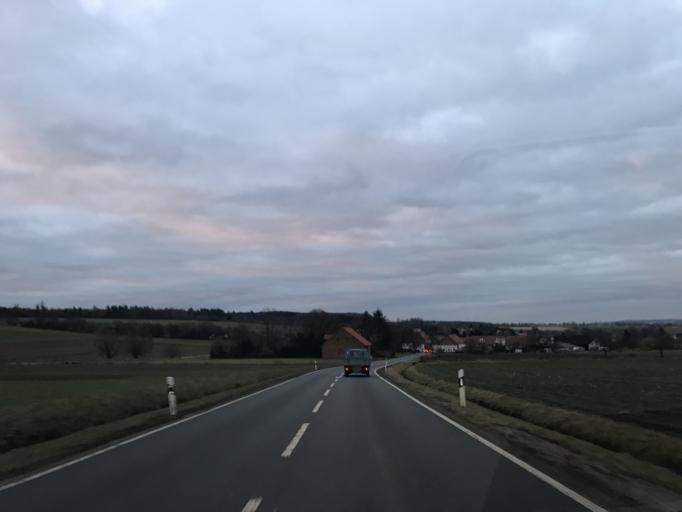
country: DE
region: Hesse
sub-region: Regierungsbezirk Kassel
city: Hofgeismar
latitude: 51.5243
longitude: 9.4170
